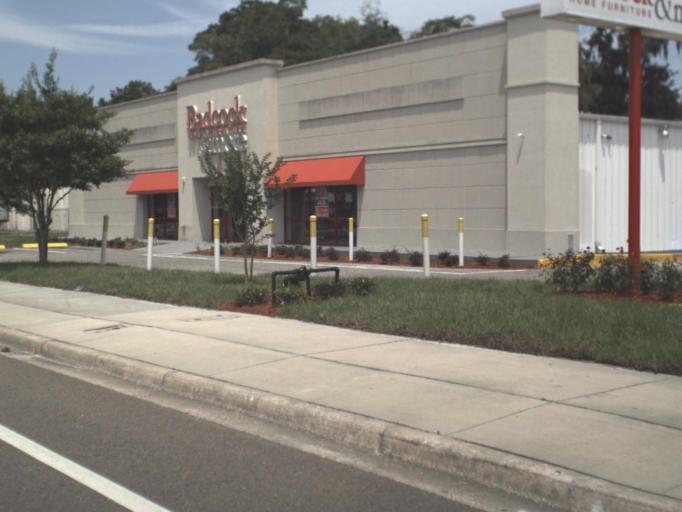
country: US
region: Florida
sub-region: Duval County
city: Jacksonville
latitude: 30.3793
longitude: -81.6504
